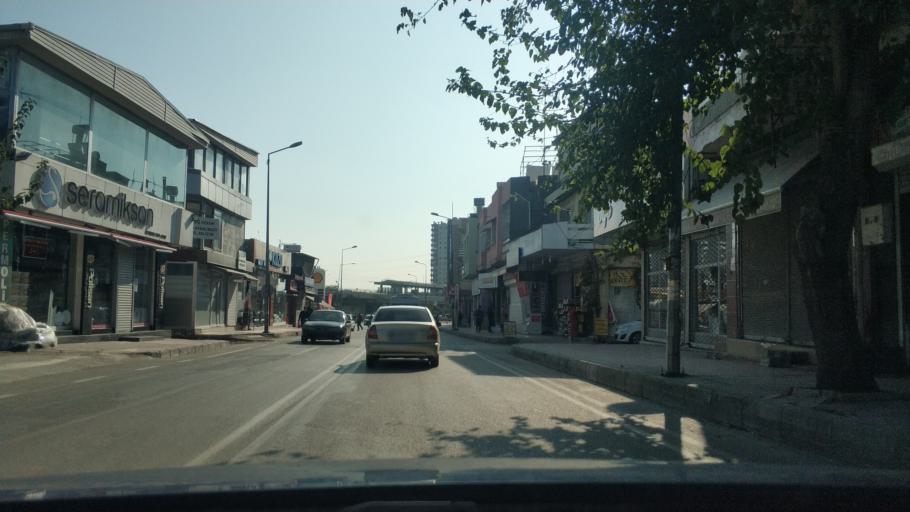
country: TR
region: Adana
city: Seyhan
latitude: 37.0142
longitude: 35.3026
